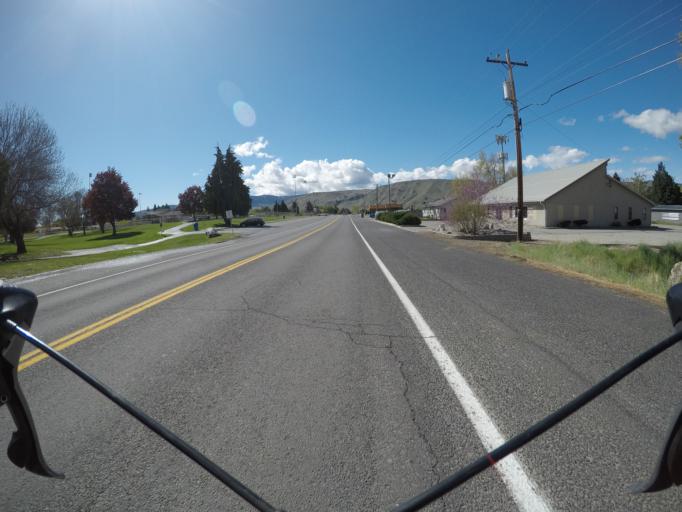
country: US
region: Washington
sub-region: Douglas County
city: East Wenatchee
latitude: 47.4082
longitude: -120.2771
